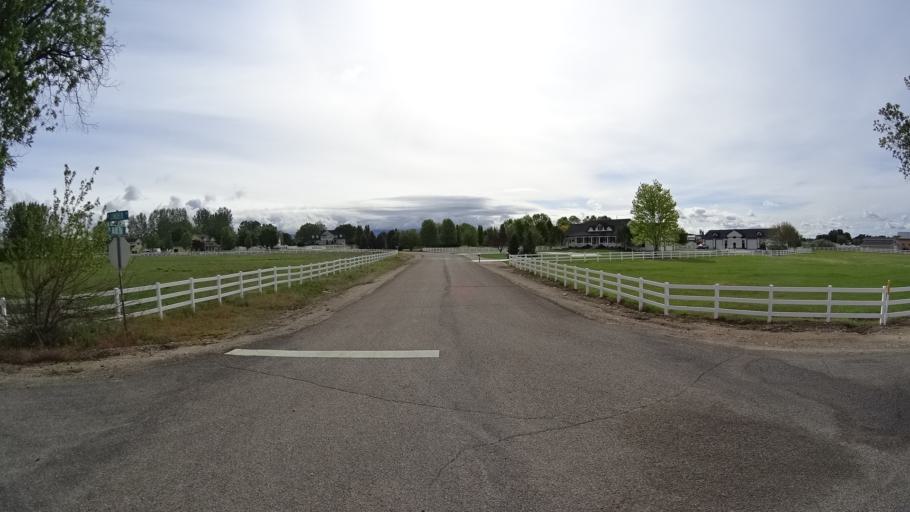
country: US
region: Idaho
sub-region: Ada County
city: Eagle
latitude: 43.7293
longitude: -116.4134
